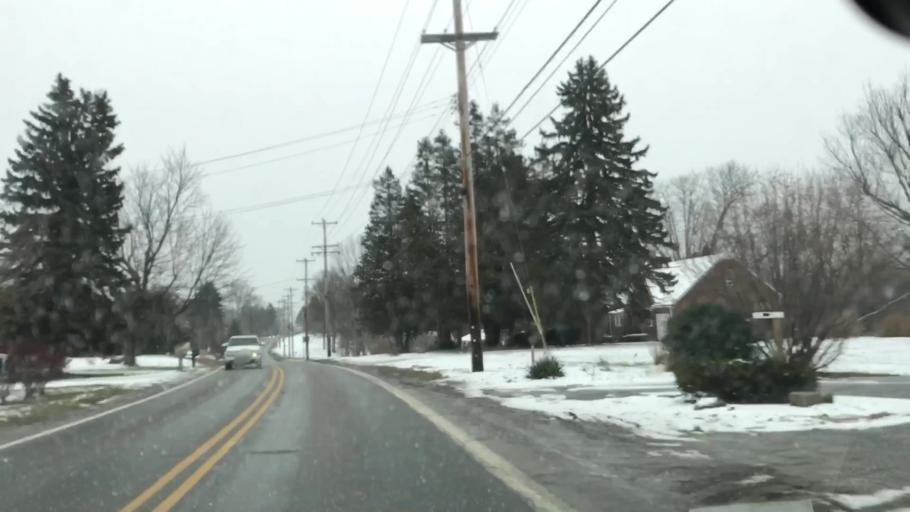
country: US
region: Pennsylvania
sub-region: Beaver County
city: Industry
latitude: 40.6965
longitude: -80.3857
